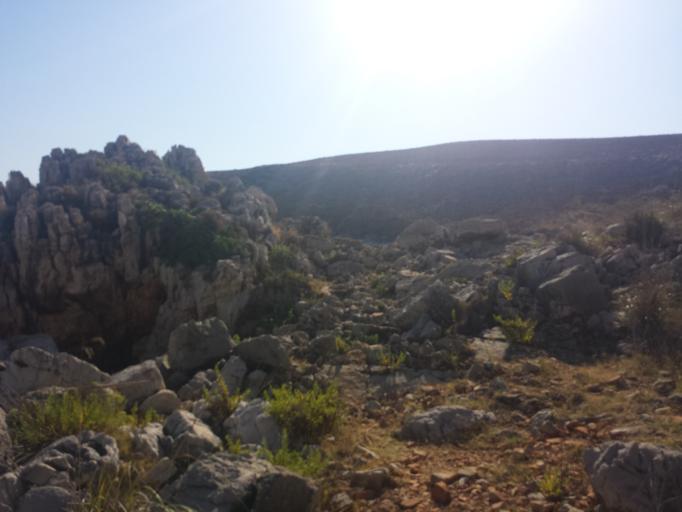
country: IT
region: Sicily
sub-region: Trapani
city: Castellammare del Golfo
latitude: 38.0495
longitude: 12.8559
